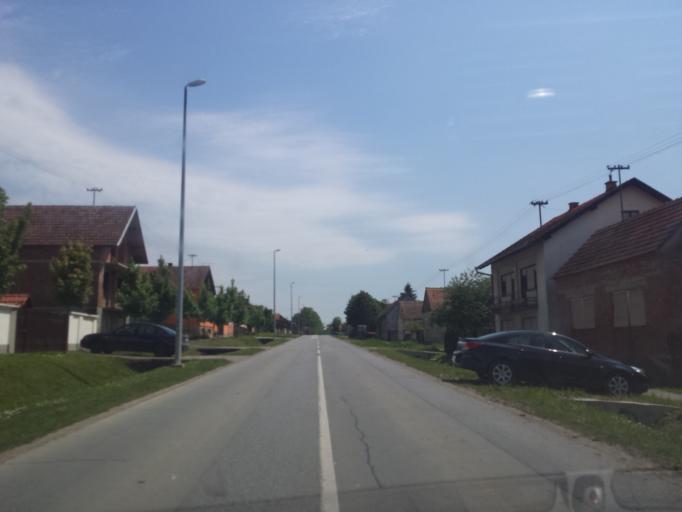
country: HR
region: Brodsko-Posavska
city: Oriovac
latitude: 45.1695
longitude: 17.8062
